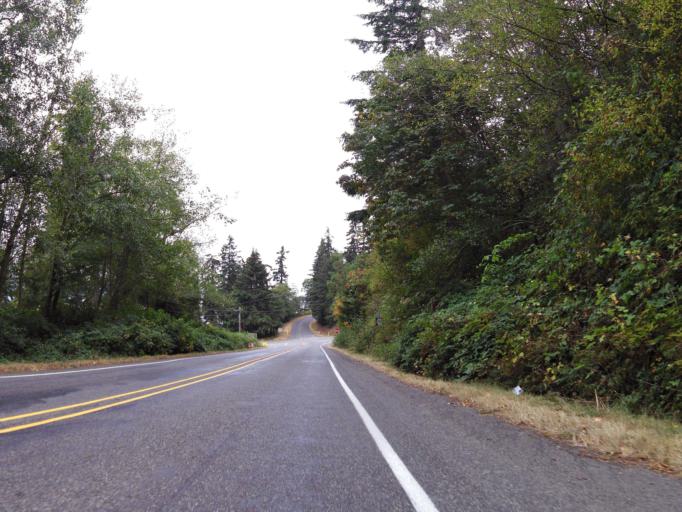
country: US
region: Washington
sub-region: Kitsap County
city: Lofall
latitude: 47.8687
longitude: -122.6383
